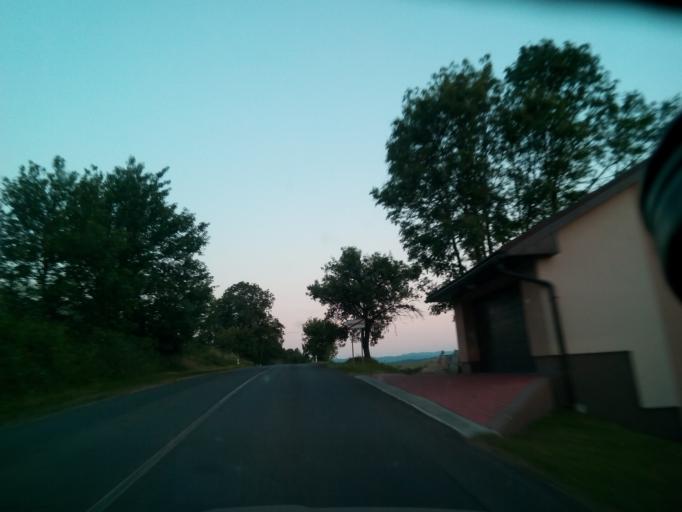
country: SK
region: Presovsky
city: Lubica
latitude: 49.0434
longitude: 20.4385
